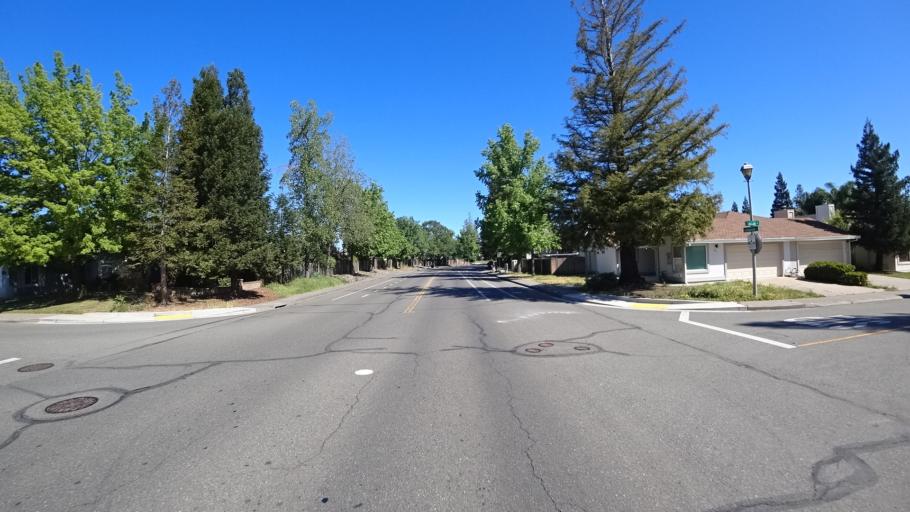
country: US
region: California
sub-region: Placer County
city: Rocklin
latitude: 38.7819
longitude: -121.2492
